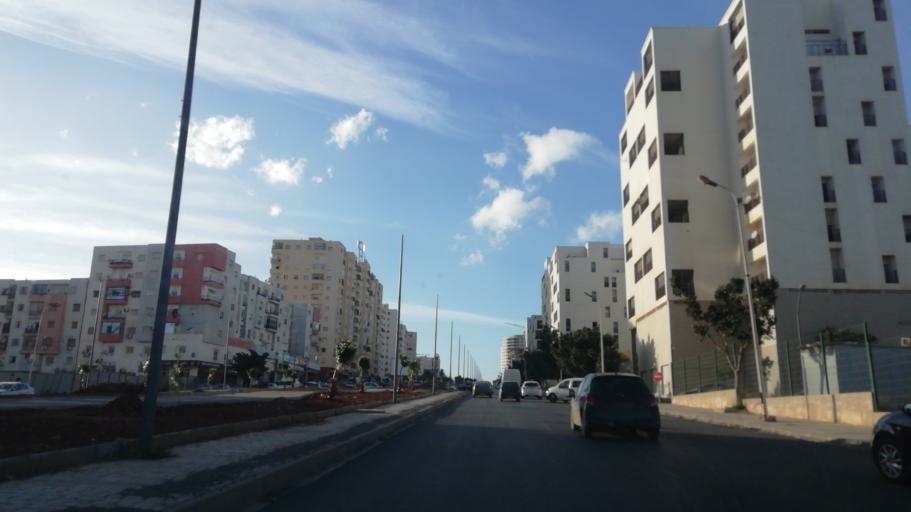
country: DZ
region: Oran
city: Bir el Djir
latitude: 35.7051
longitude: -0.5549
